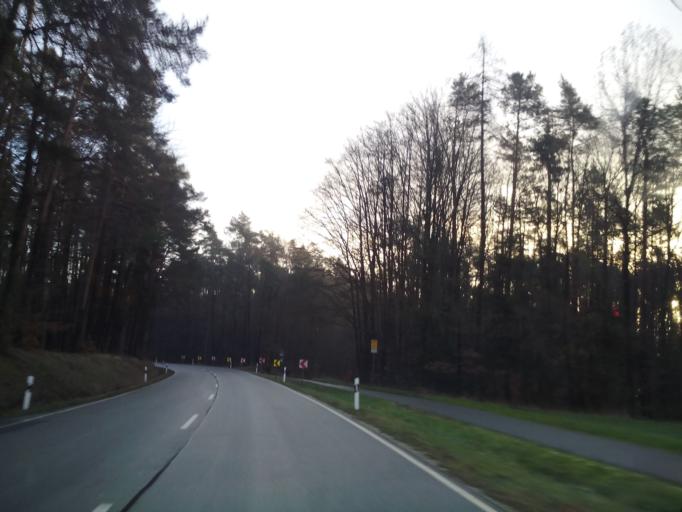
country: DE
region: Bavaria
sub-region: Upper Franconia
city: Lichtenfels
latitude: 50.1713
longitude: 11.0330
